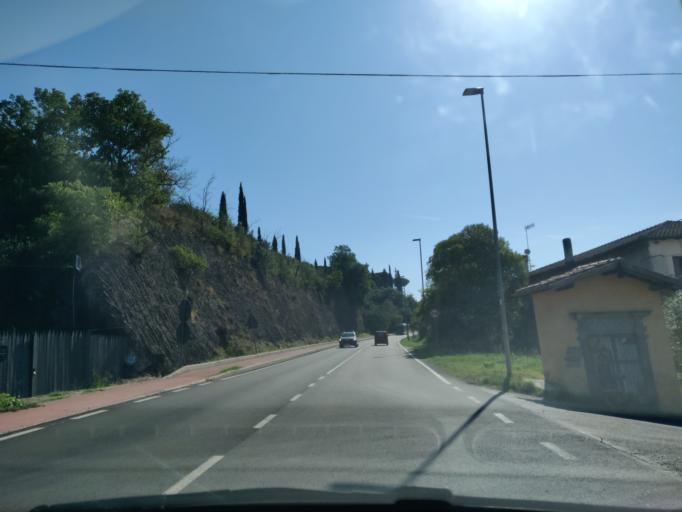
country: IT
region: Latium
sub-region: Provincia di Viterbo
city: Viterbo
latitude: 42.4190
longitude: 12.0846
